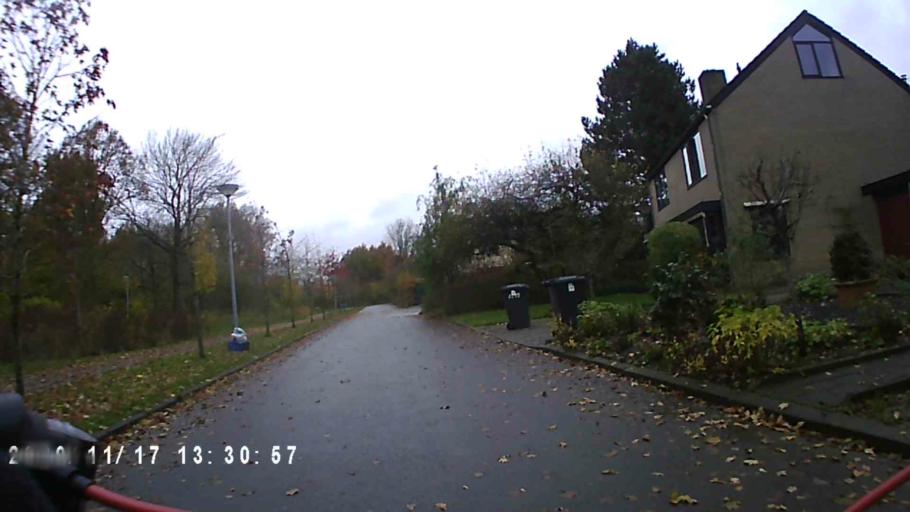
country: NL
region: Groningen
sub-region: Gemeente Zuidhorn
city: Zuidhorn
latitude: 53.2491
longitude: 6.3959
